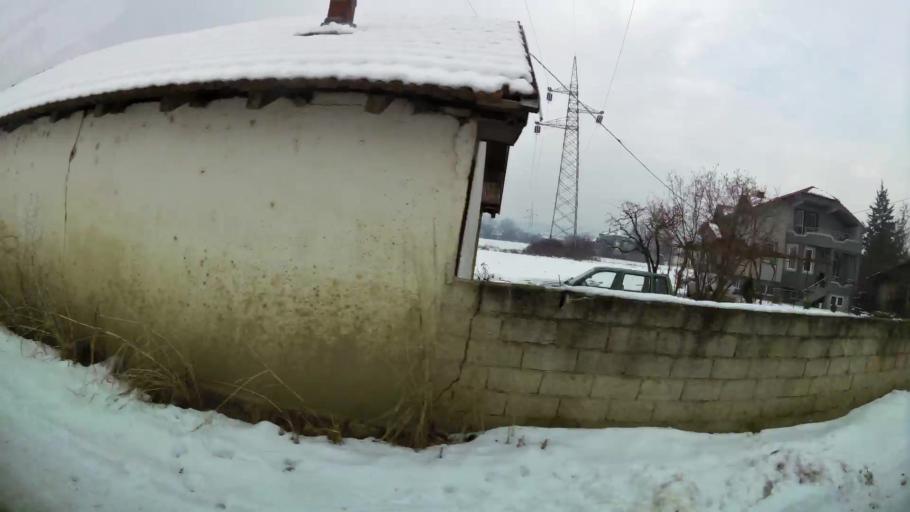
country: MK
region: Saraj
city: Saraj
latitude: 42.0428
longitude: 21.3566
